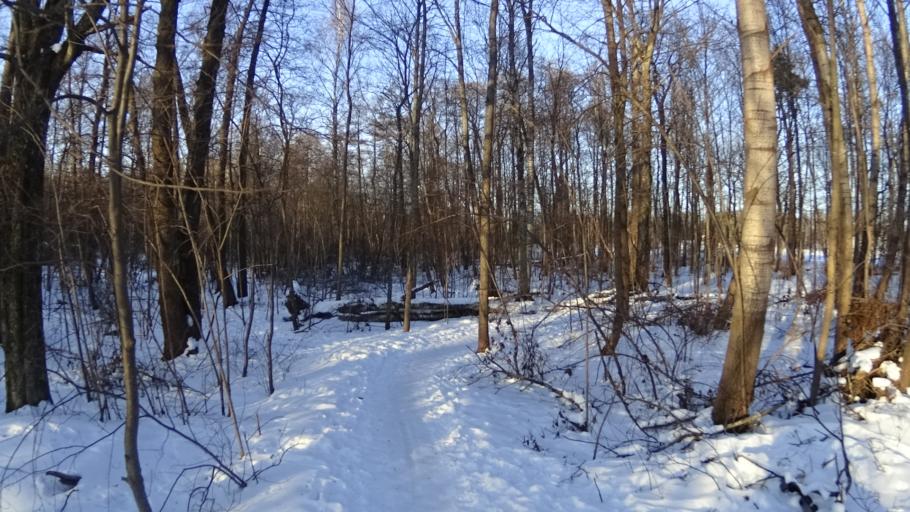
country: FI
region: Uusimaa
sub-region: Helsinki
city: Teekkarikylae
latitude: 60.2104
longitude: 24.8522
